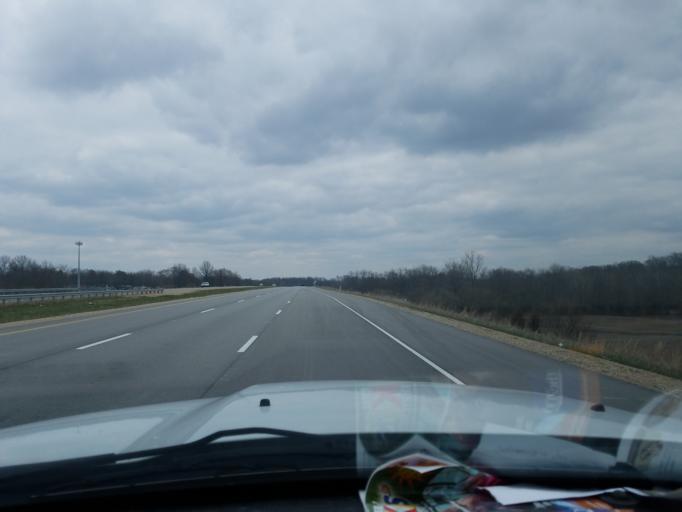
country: US
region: Indiana
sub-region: Vigo County
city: Terre Haute
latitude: 39.4009
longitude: -87.3697
